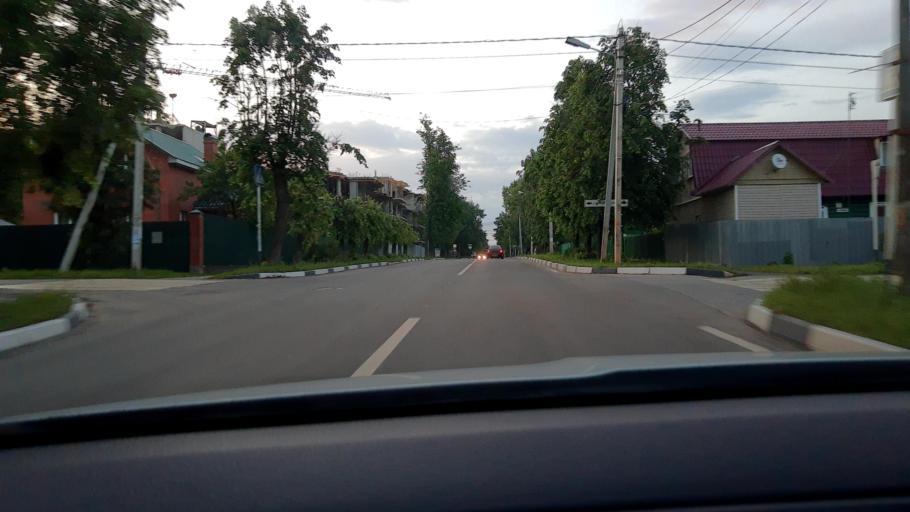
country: RU
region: Moskovskaya
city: Zvenigorod
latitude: 55.7338
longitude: 36.8605
